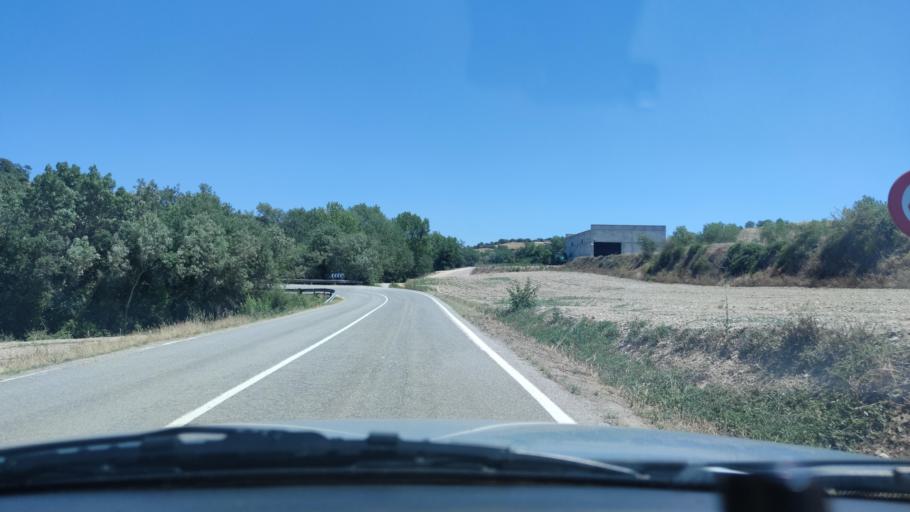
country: ES
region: Catalonia
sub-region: Provincia de Lleida
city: Ivorra
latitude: 41.7687
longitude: 1.3953
